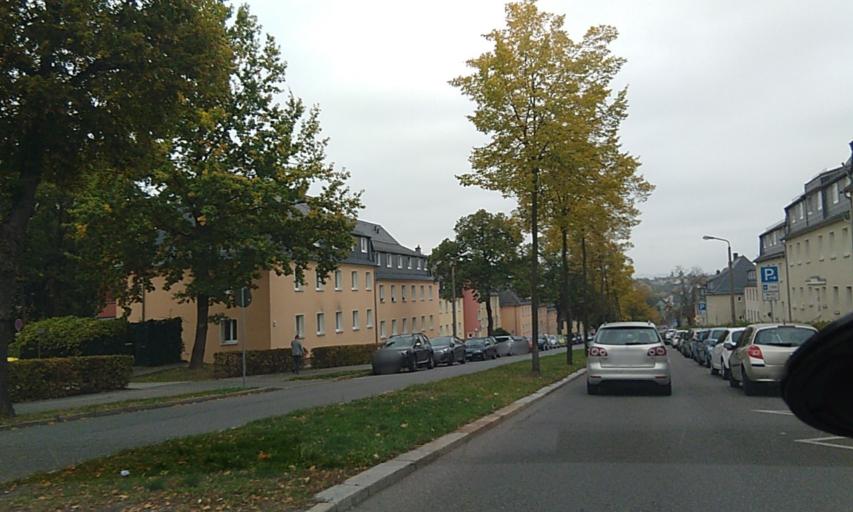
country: DE
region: Saxony
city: Wittgensdorf
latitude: 50.8432
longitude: 12.8857
